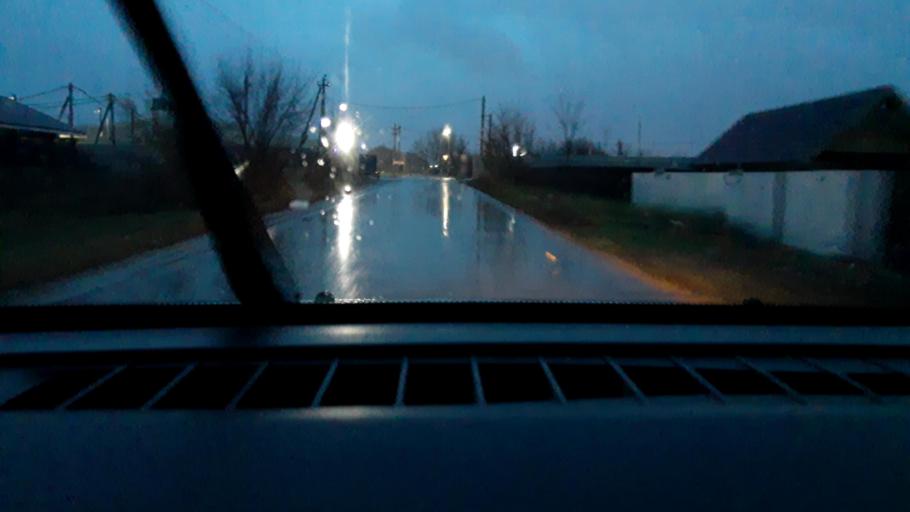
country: RU
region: Nizjnij Novgorod
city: Afonino
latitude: 56.2027
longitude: 44.1326
